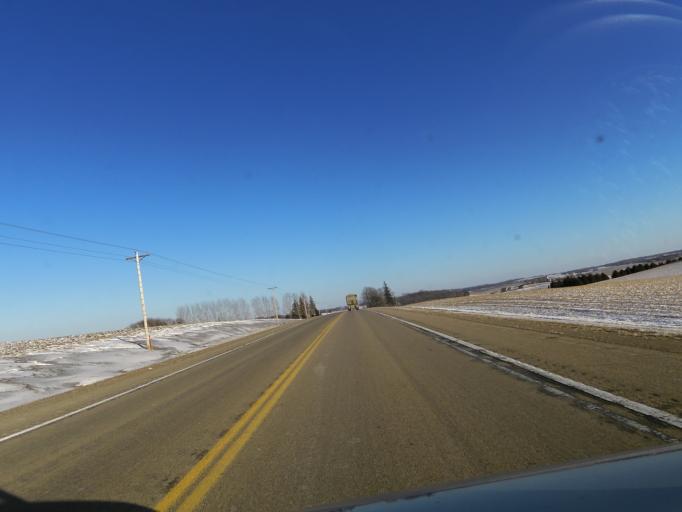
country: US
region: Minnesota
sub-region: Rice County
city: Lonsdale
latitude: 44.4860
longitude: -93.4988
